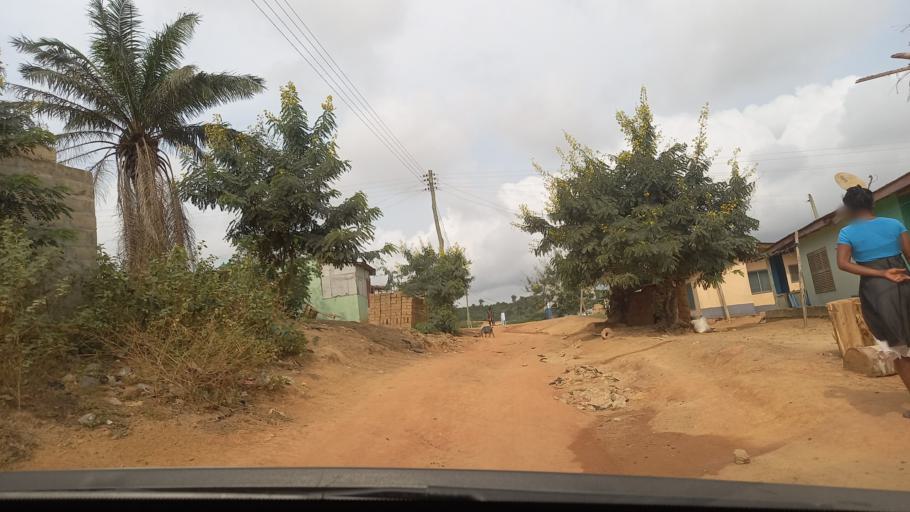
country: GH
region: Western
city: Shama Junction
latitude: 4.9863
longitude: -1.6391
